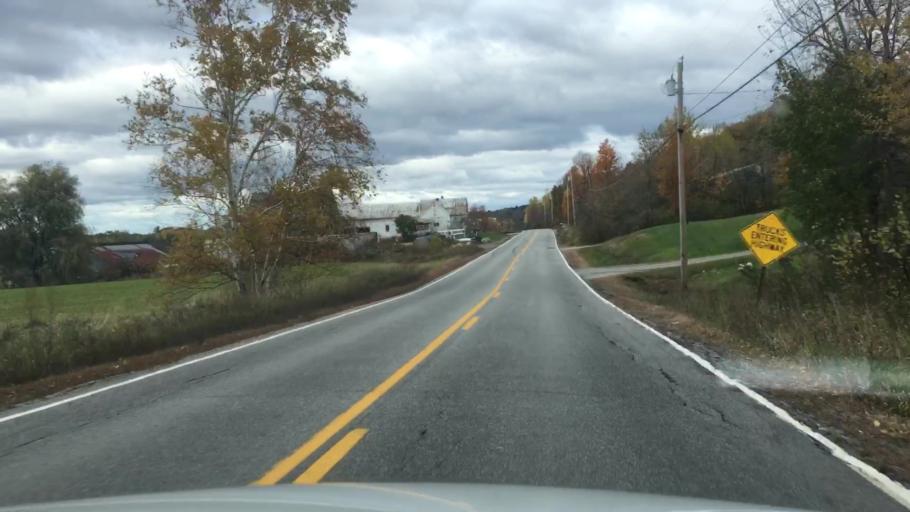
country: US
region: Maine
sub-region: Androscoggin County
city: Sabattus
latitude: 44.1441
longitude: -70.0860
